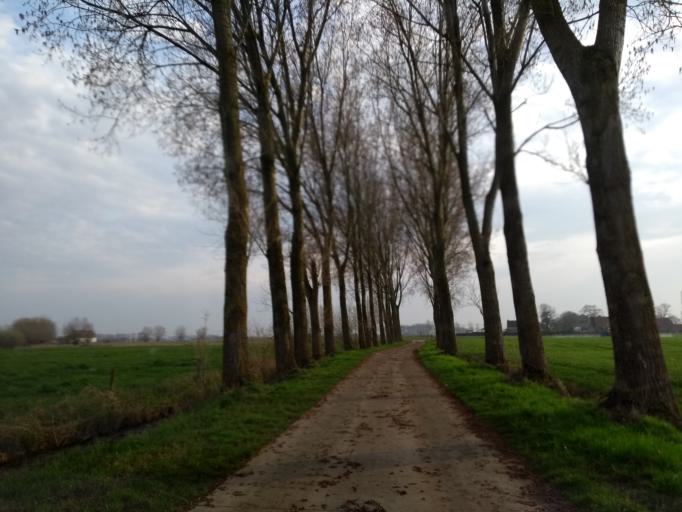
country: BE
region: Flanders
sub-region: Provincie Oost-Vlaanderen
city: Nevele
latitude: 51.0569
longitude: 3.5021
